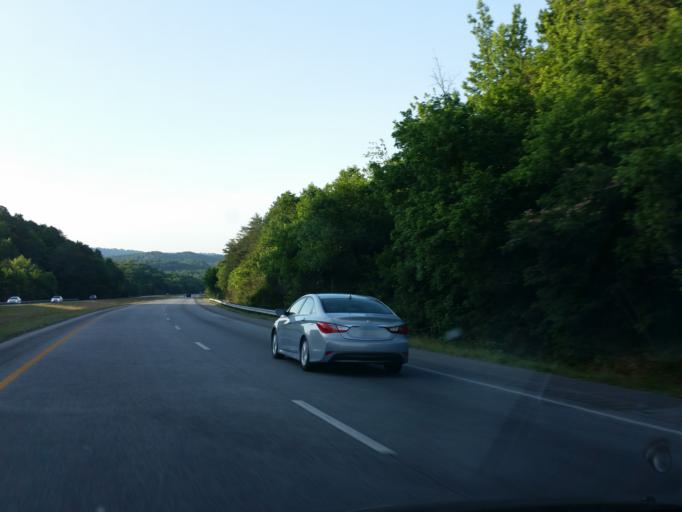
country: US
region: Georgia
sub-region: Dade County
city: Trenton
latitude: 34.8001
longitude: -85.5500
